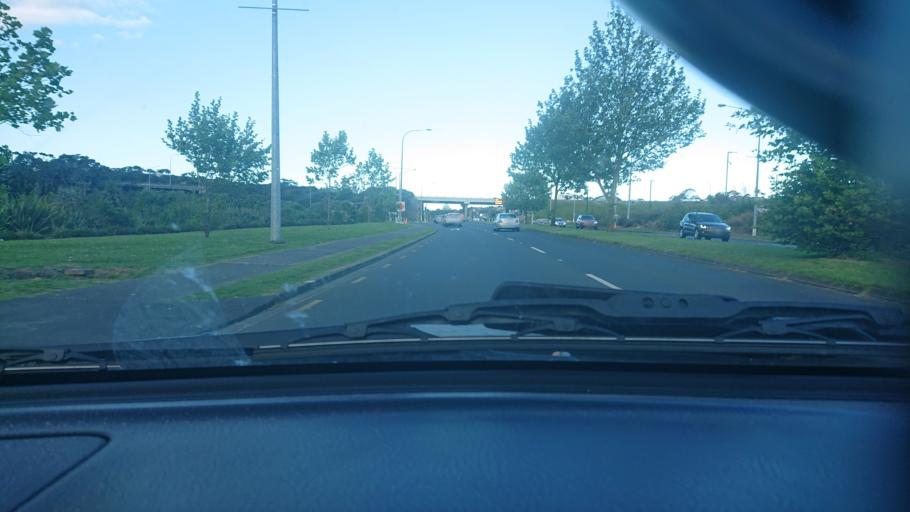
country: NZ
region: Auckland
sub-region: Auckland
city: Rothesay Bay
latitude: -36.7196
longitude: 174.7106
